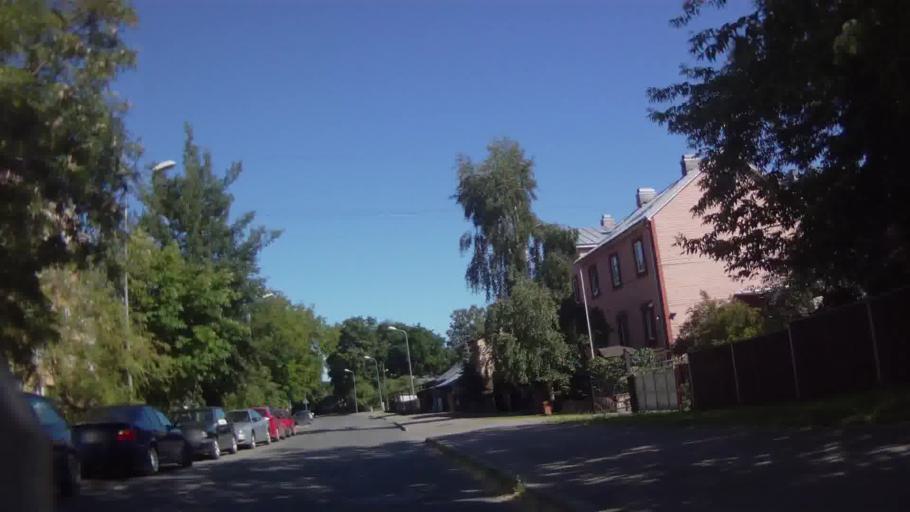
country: LV
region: Riga
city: Riga
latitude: 56.9151
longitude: 24.1007
